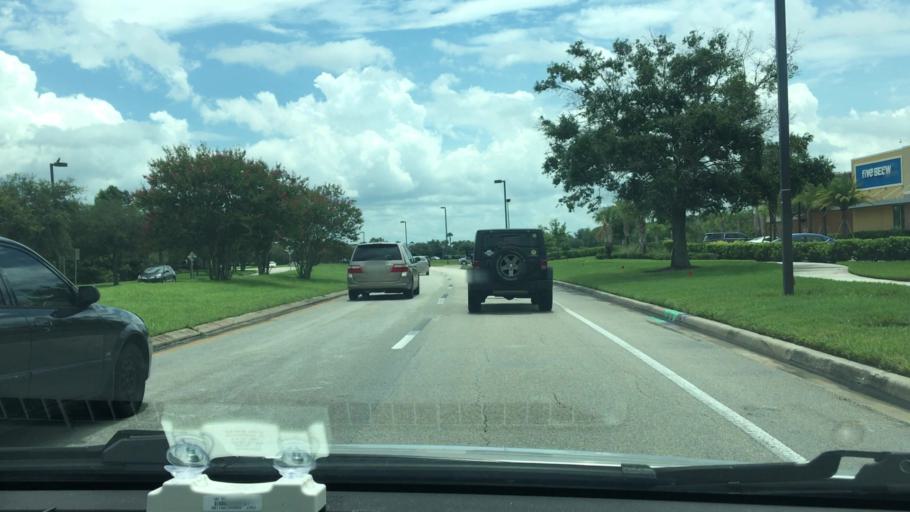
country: US
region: Florida
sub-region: Orange County
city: Conway
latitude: 28.4669
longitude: -81.3043
